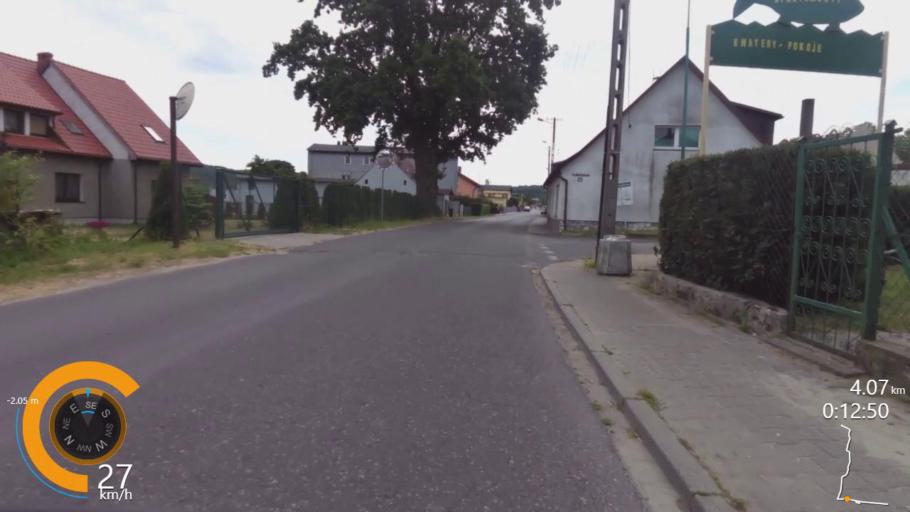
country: PL
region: West Pomeranian Voivodeship
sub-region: Powiat kamienski
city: Miedzyzdroje
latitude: 53.8806
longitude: 14.4361
